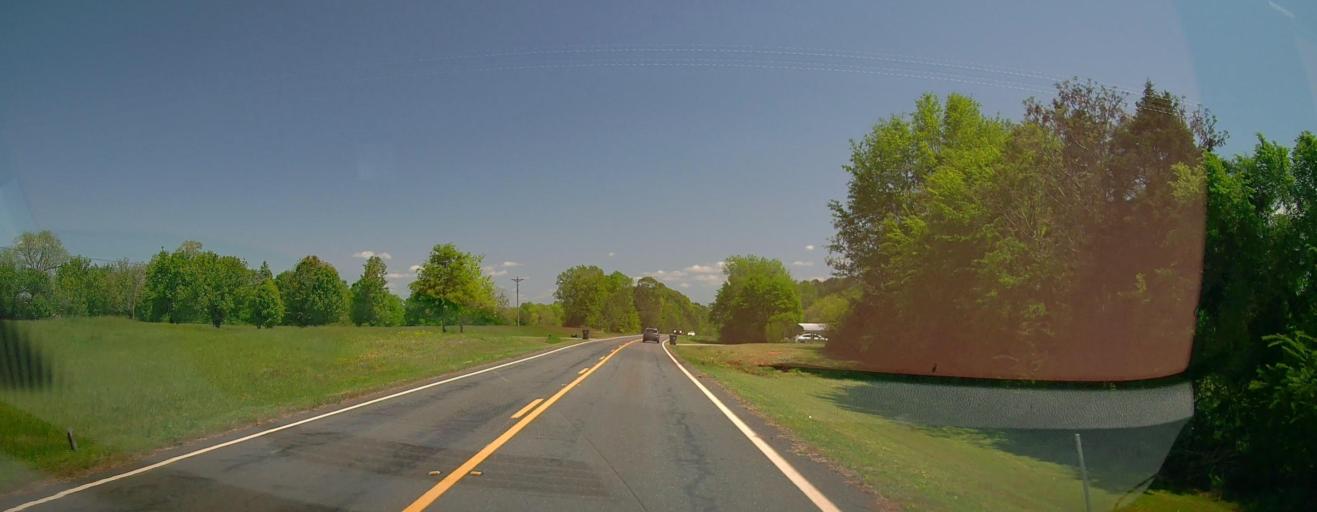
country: US
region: Georgia
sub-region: Jasper County
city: Monticello
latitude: 33.2729
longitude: -83.5927
